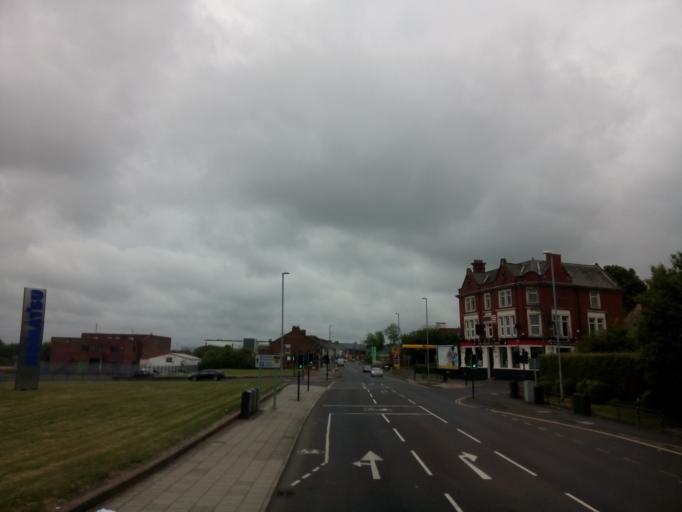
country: GB
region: England
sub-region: County Durham
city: Chester-le-Street
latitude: 54.8916
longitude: -1.5770
